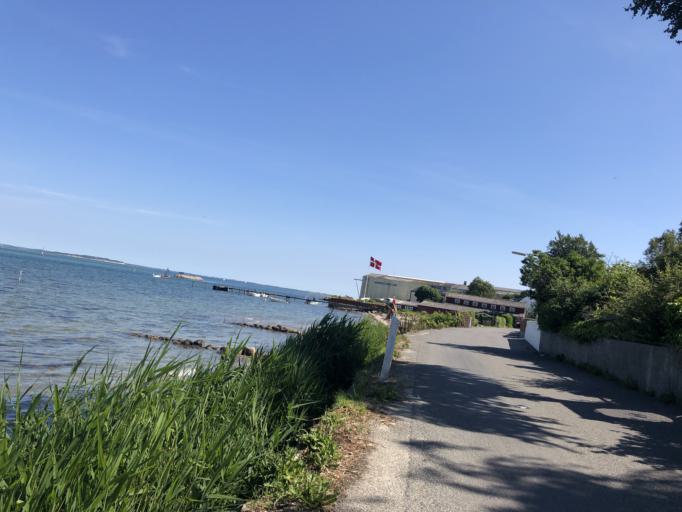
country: DK
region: South Denmark
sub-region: AEro Kommune
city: Marstal
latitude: 54.8595
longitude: 10.5189
